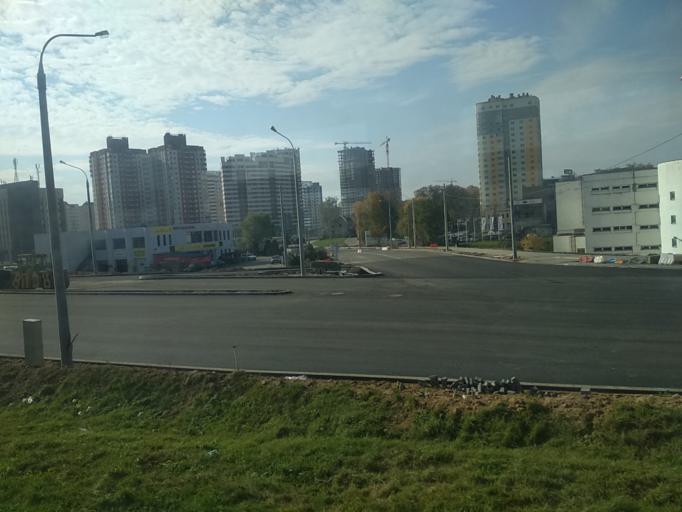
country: BY
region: Minsk
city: Minsk
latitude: 53.8733
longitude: 27.5620
